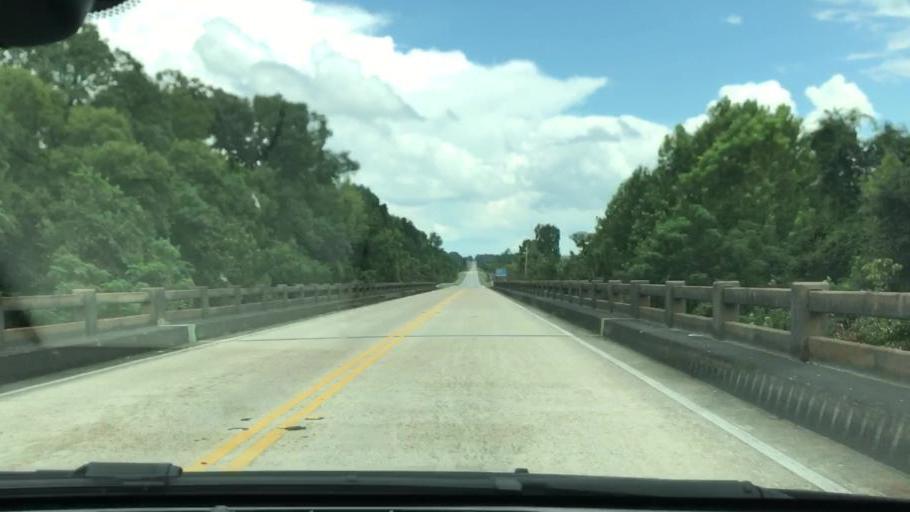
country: US
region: Georgia
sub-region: Seminole County
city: Donalsonville
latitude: 30.9775
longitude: -85.0050
